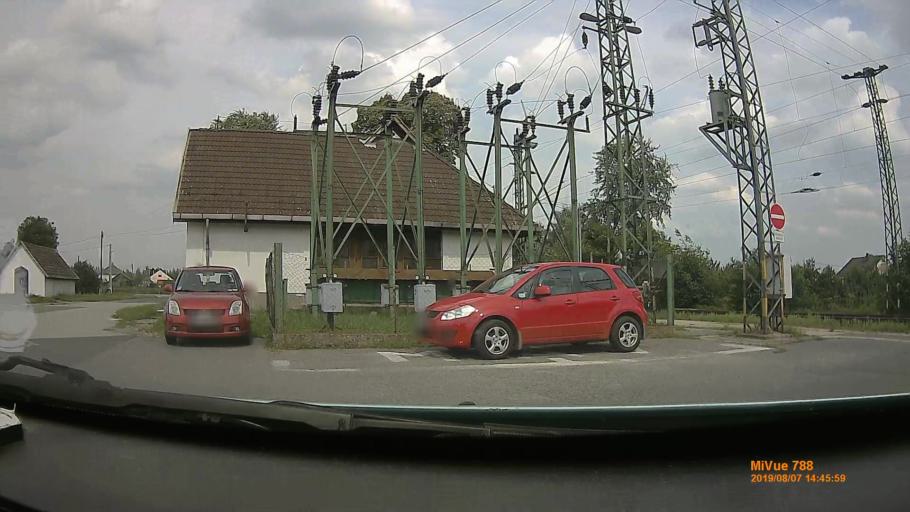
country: HU
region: Borsod-Abauj-Zemplen
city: Halmaj
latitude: 48.2464
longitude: 20.9911
